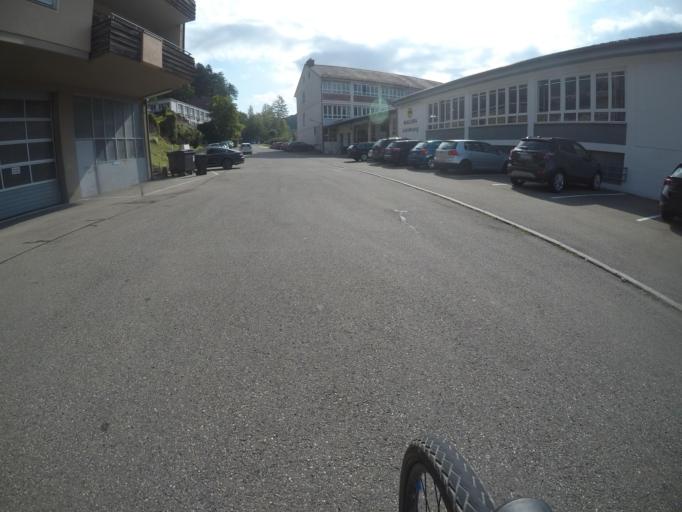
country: DE
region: Baden-Wuerttemberg
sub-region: Tuebingen Region
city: Bad Urach
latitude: 48.4956
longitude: 9.3943
